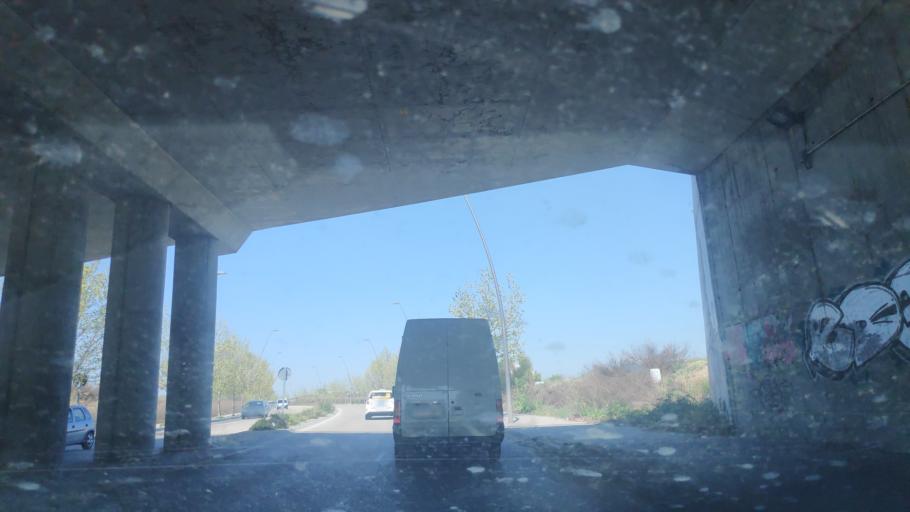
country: ES
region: Madrid
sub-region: Provincia de Madrid
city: Pinto
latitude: 40.2900
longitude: -3.6820
